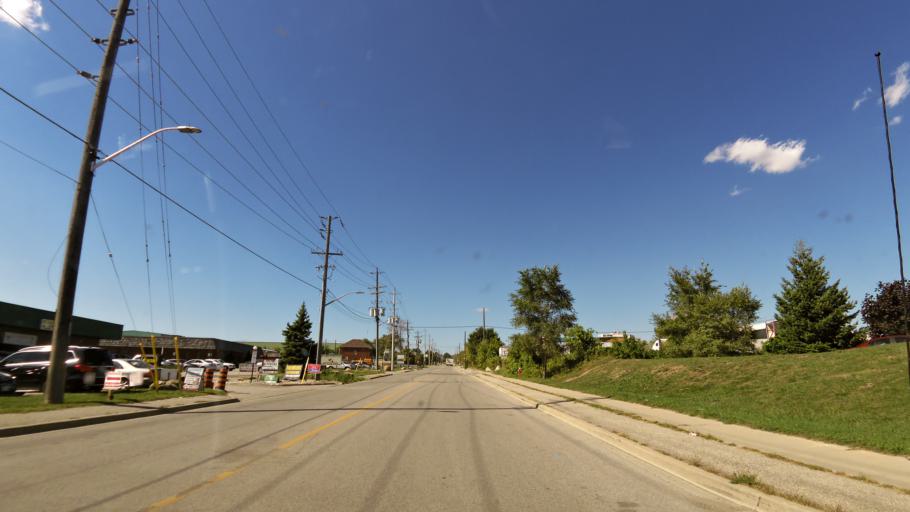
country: CA
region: Ontario
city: Etobicoke
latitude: 43.5936
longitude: -79.5912
